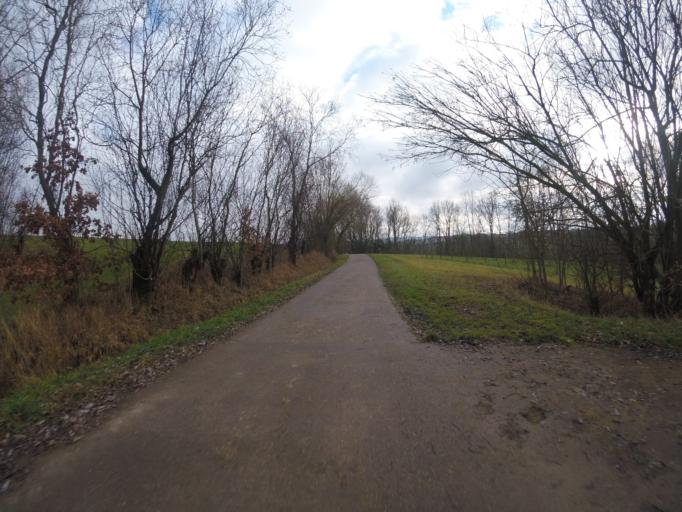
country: DE
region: Baden-Wuerttemberg
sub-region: Regierungsbezirk Stuttgart
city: Allmersbach im Tal
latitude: 48.9382
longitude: 9.4707
